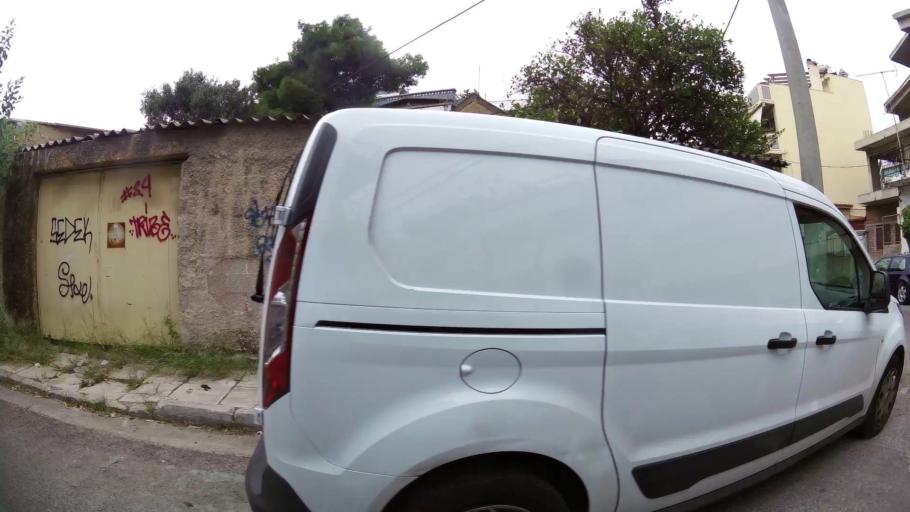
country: GR
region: Attica
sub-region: Nomarchia Athinas
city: Peristeri
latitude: 38.0011
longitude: 23.6835
